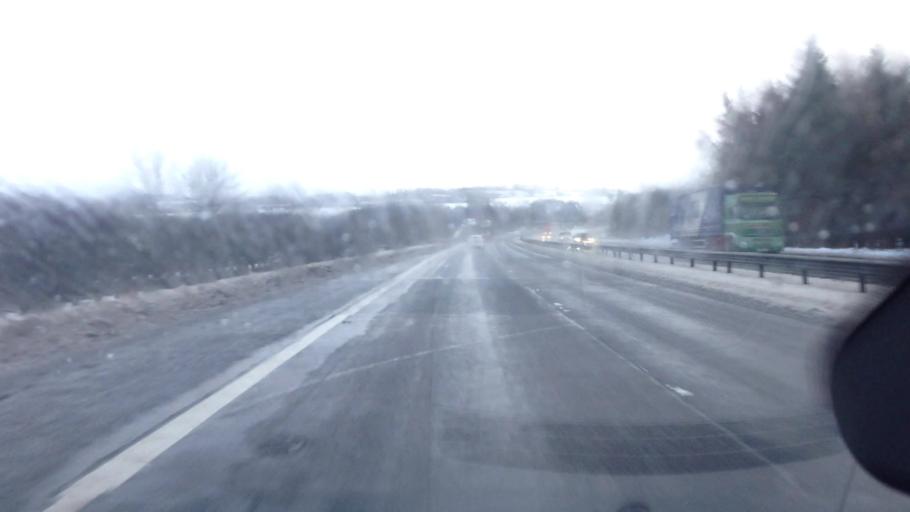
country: GB
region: Scotland
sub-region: South Lanarkshire
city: Blackwood
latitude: 55.6547
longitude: -3.8994
